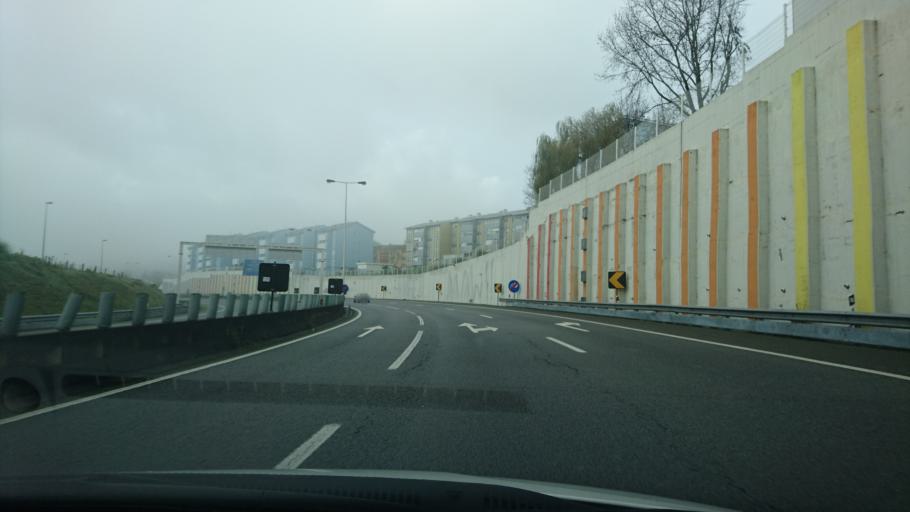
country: PT
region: Porto
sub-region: Gondomar
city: Rio Tinto
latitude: 41.1585
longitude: -8.5682
